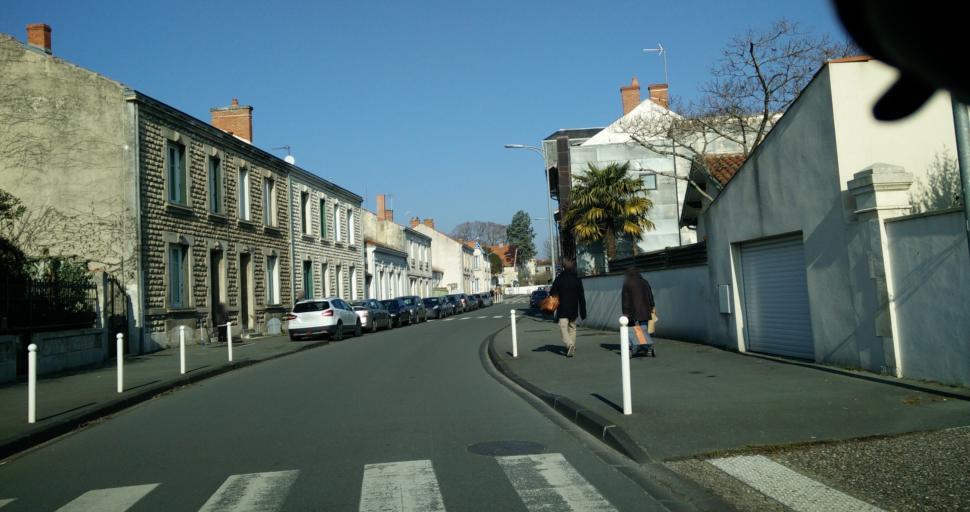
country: FR
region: Poitou-Charentes
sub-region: Departement de la Charente-Maritime
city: La Rochelle
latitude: 46.1648
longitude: -1.1592
